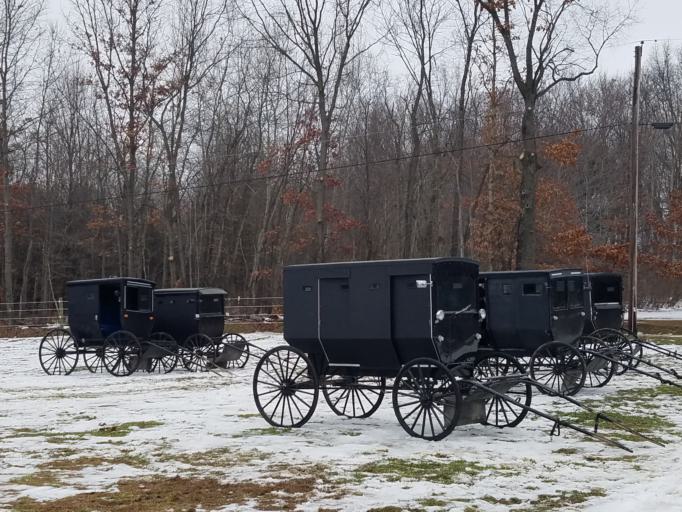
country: US
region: Pennsylvania
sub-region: Mercer County
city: Mercer
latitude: 41.3487
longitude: -80.2527
